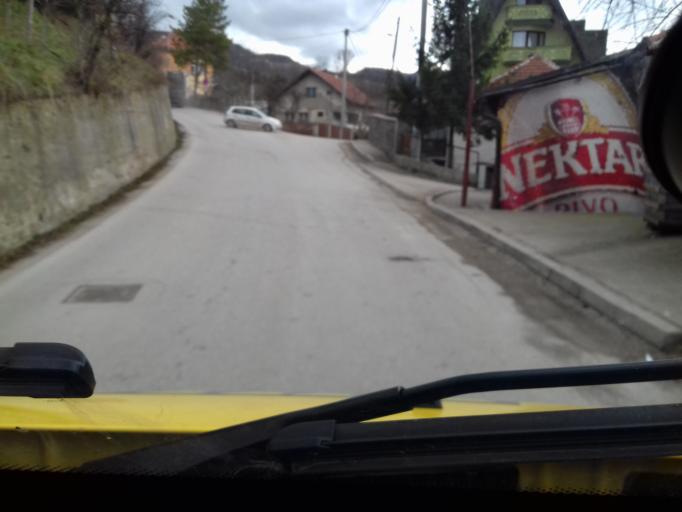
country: BA
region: Federation of Bosnia and Herzegovina
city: Zenica
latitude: 44.1699
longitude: 17.9768
